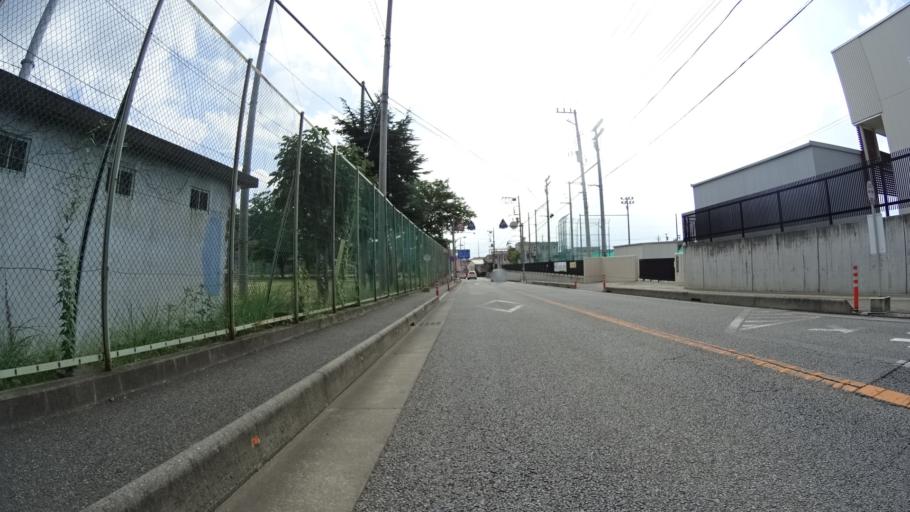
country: JP
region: Yamanashi
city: Kofu-shi
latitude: 35.6794
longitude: 138.5664
